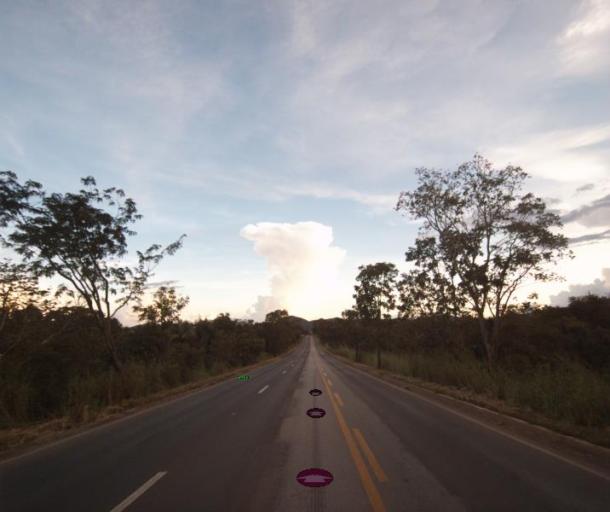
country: BR
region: Goias
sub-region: Uruacu
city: Uruacu
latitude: -14.3478
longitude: -49.1577
